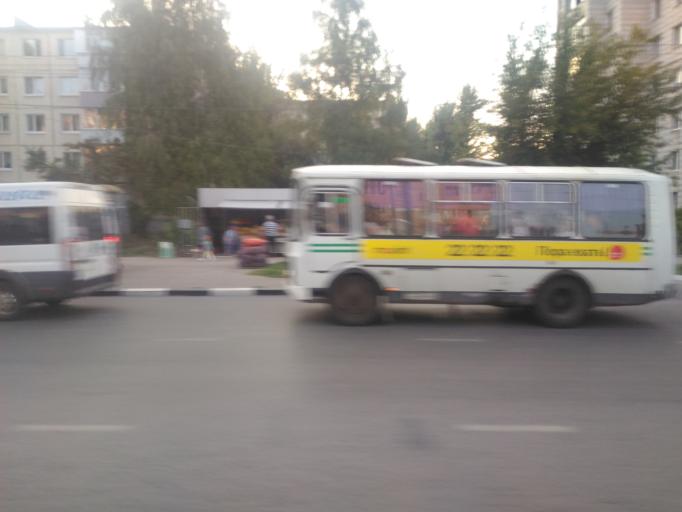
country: RU
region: Ulyanovsk
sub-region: Ulyanovskiy Rayon
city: Ulyanovsk
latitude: 54.2717
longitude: 48.2870
